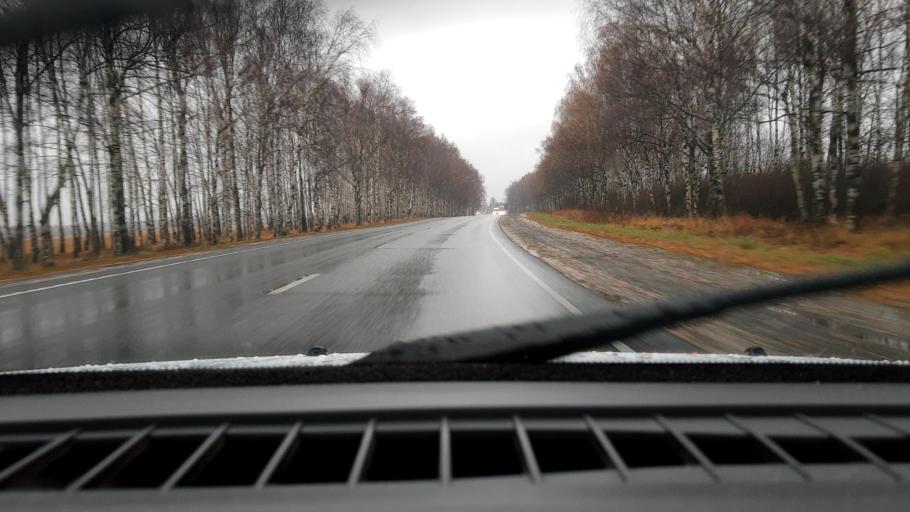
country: RU
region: Nizjnij Novgorod
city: Sitniki
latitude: 56.5370
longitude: 44.0211
